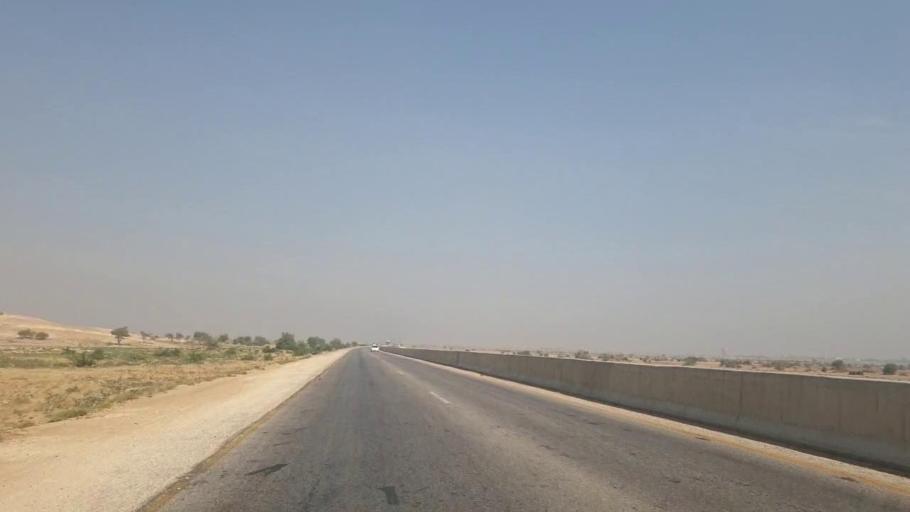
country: PK
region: Sindh
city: Jamshoro
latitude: 25.5533
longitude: 68.2993
